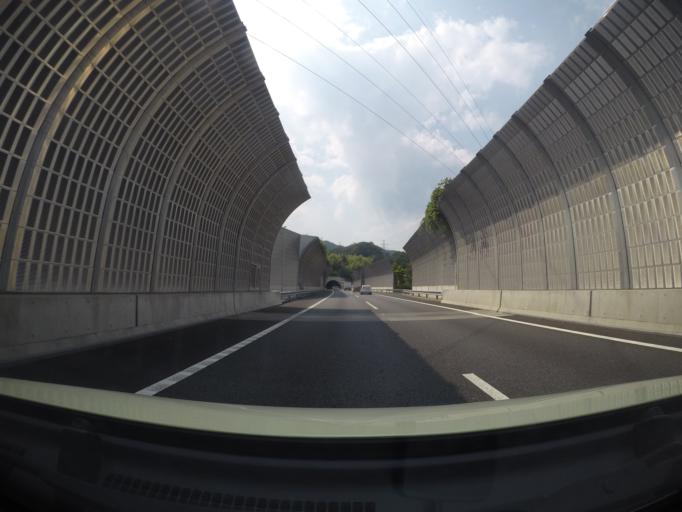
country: JP
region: Tokyo
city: Hachioji
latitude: 35.5955
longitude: 139.2810
